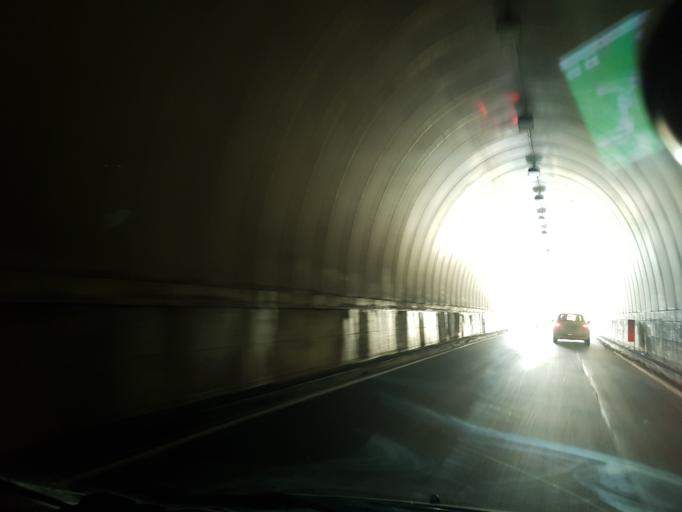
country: IT
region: Tuscany
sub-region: Provincia di Lucca
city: Minucciano
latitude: 44.1648
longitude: 10.2121
